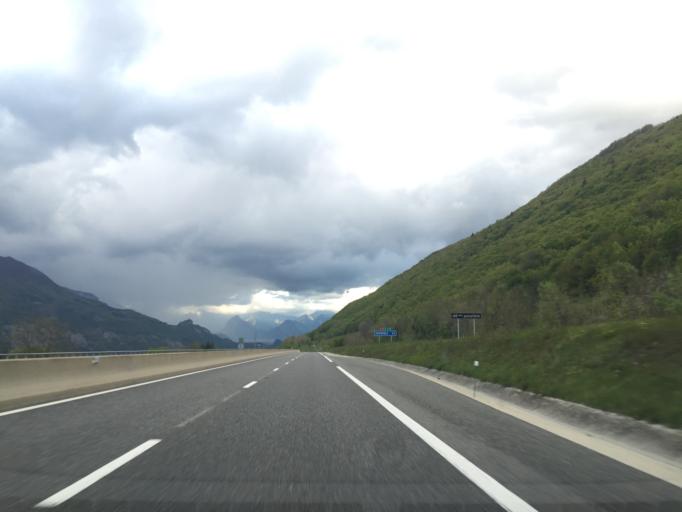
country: FR
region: Rhone-Alpes
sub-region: Departement de l'Isere
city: Le Gua
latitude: 44.9996
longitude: 5.6538
